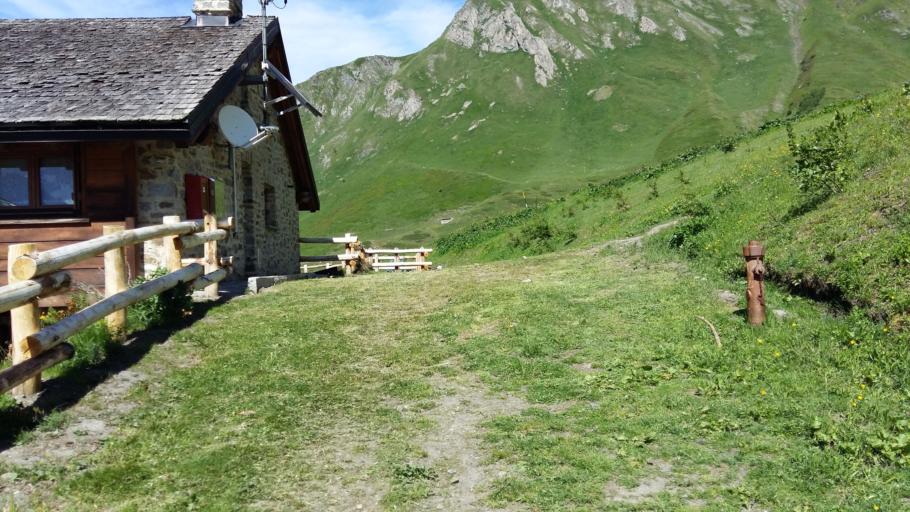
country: IT
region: Aosta Valley
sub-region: Valle d'Aosta
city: Courmayeur
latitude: 45.8467
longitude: 7.0336
